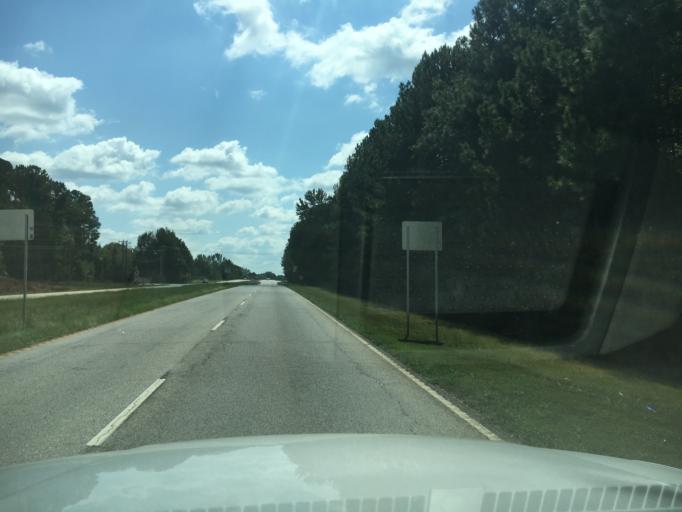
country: US
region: South Carolina
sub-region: Greenwood County
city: Ware Shoals
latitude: 34.3186
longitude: -82.2238
